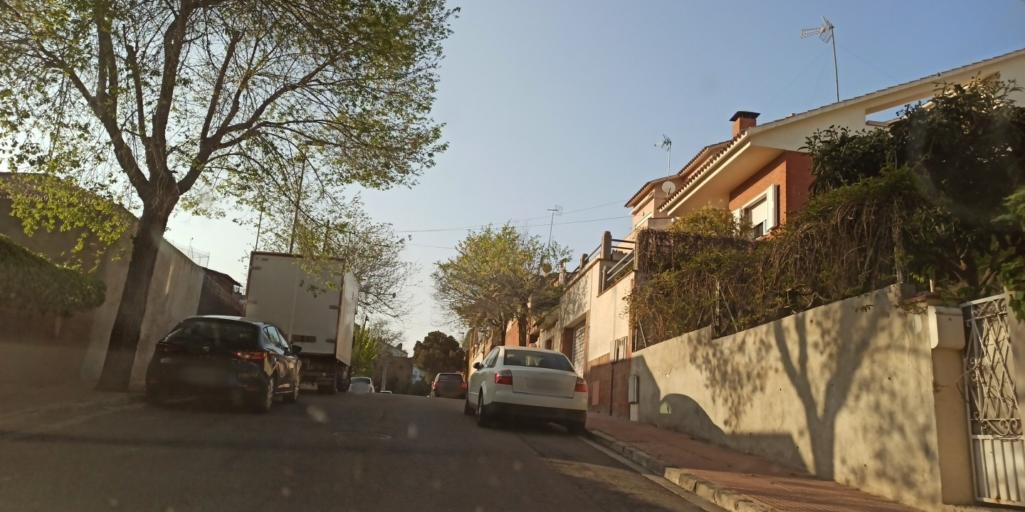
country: ES
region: Catalonia
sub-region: Provincia de Barcelona
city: Esplugues de Llobregat
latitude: 41.3856
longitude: 2.0861
